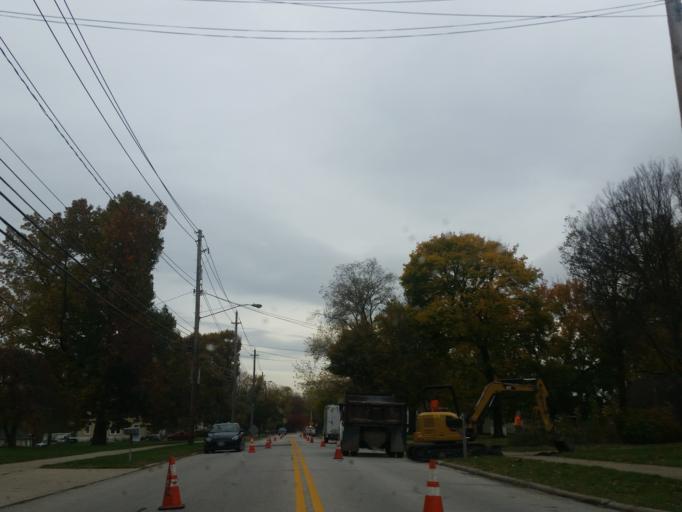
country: US
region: Ohio
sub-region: Cuyahoga County
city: Brooklyn Heights
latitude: 41.4171
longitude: -81.6677
